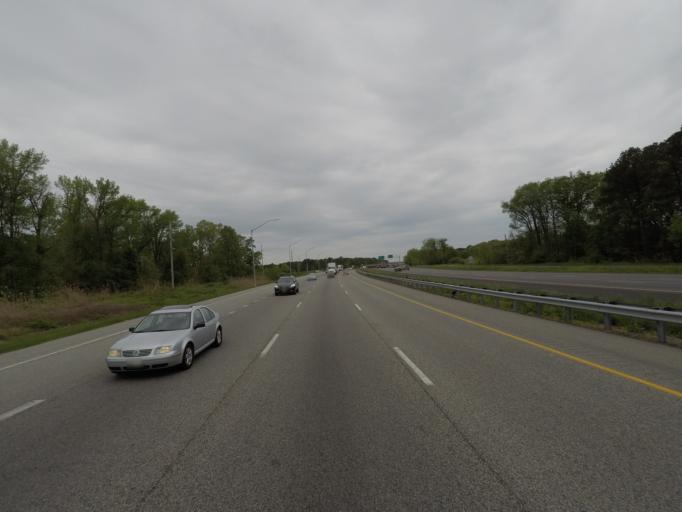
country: US
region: Maryland
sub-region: Queen Anne's County
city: Grasonville
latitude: 38.9705
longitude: -76.1790
